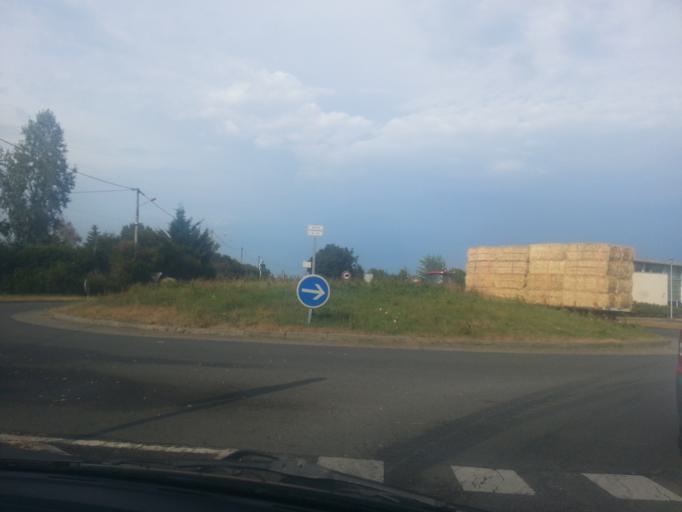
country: FR
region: Auvergne
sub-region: Departement de l'Allier
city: Bellerive-sur-Allier
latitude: 46.1099
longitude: 3.3819
